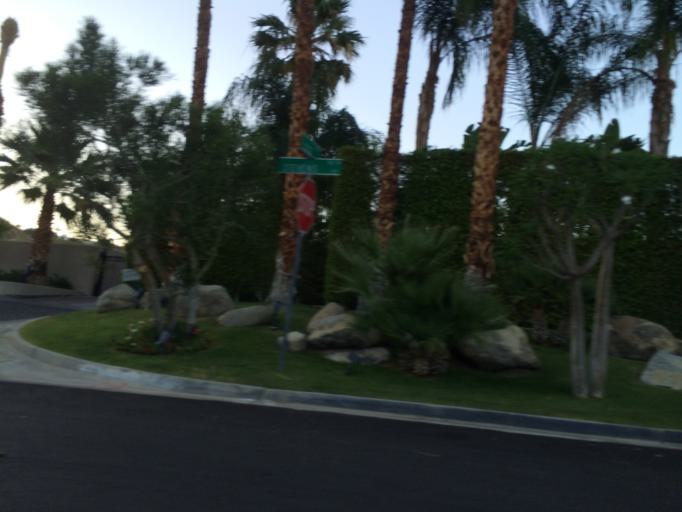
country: US
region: California
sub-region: Riverside County
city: Palm Springs
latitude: 33.8416
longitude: -116.5582
